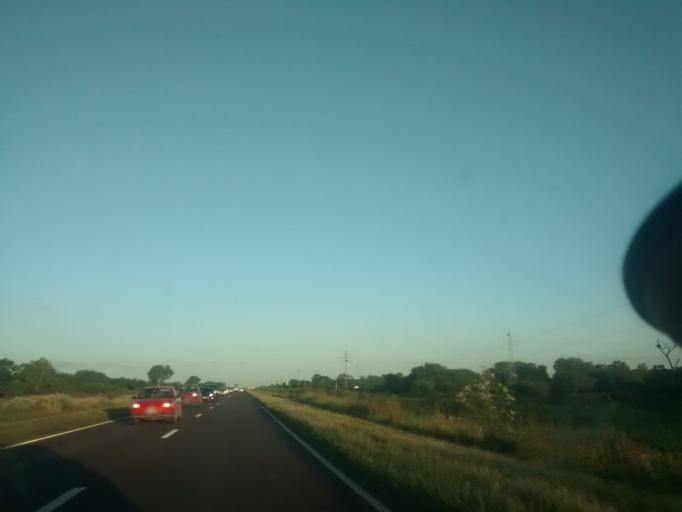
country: AR
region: Chaco
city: Colonia Elisa
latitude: -27.0841
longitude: -59.6513
